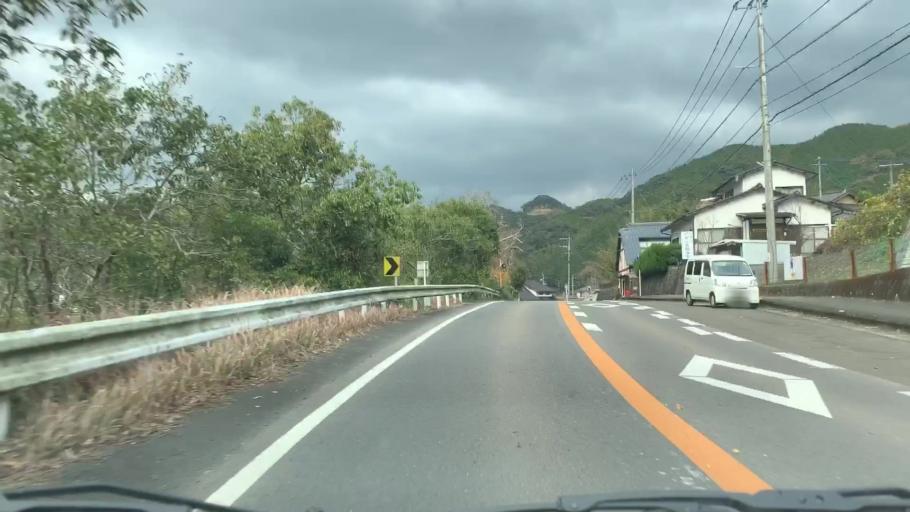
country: JP
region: Saga Prefecture
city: Ureshinomachi-shimojuku
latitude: 33.1321
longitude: 130.0307
